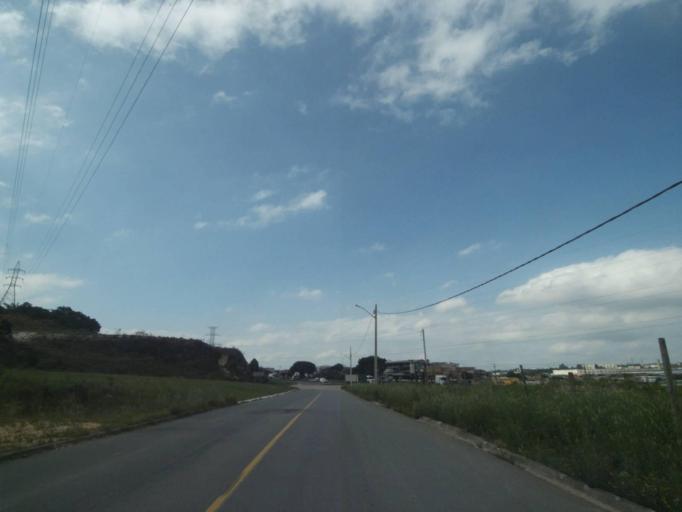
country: BR
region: Parana
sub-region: Curitiba
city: Curitiba
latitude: -25.5106
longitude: -49.3401
